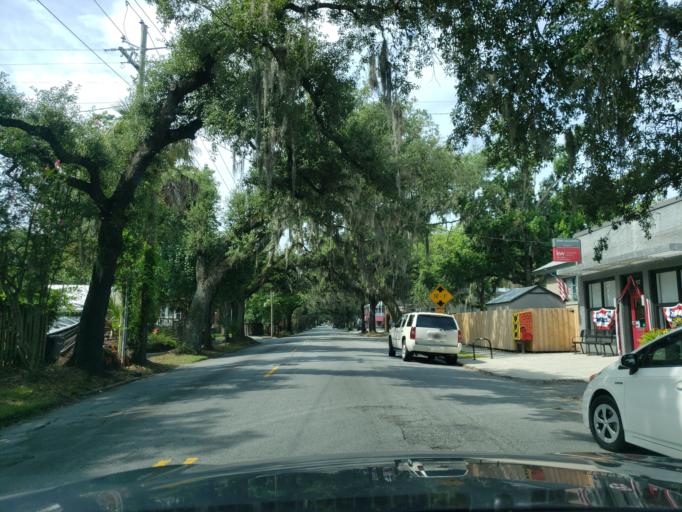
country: US
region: Georgia
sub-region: Chatham County
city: Thunderbolt
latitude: 32.0449
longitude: -81.0865
